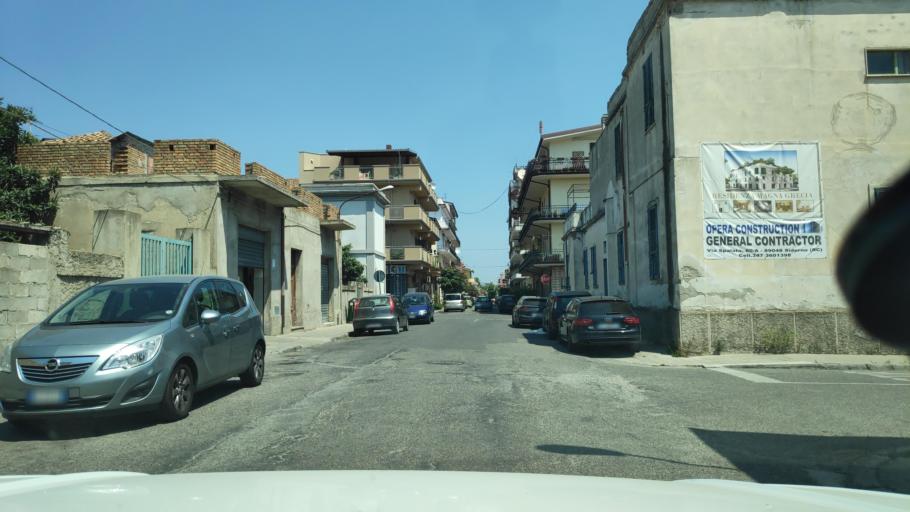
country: IT
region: Calabria
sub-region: Provincia di Reggio Calabria
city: Siderno
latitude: 38.2704
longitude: 16.2963
